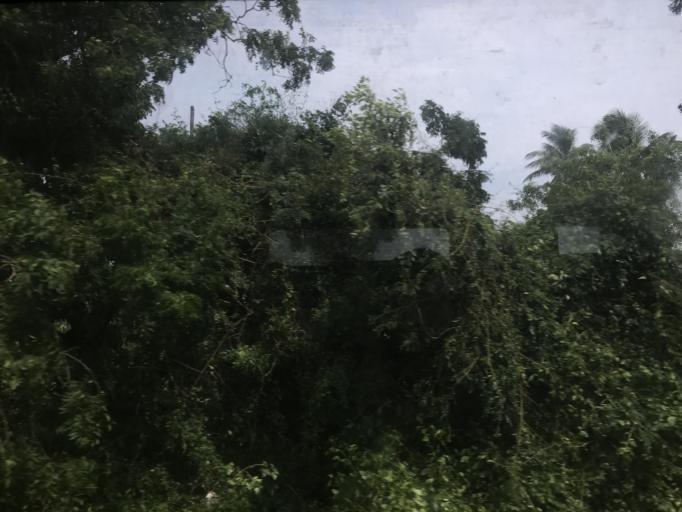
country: LK
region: Northern Province
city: Kilinochchi
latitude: 9.5855
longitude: 80.3502
